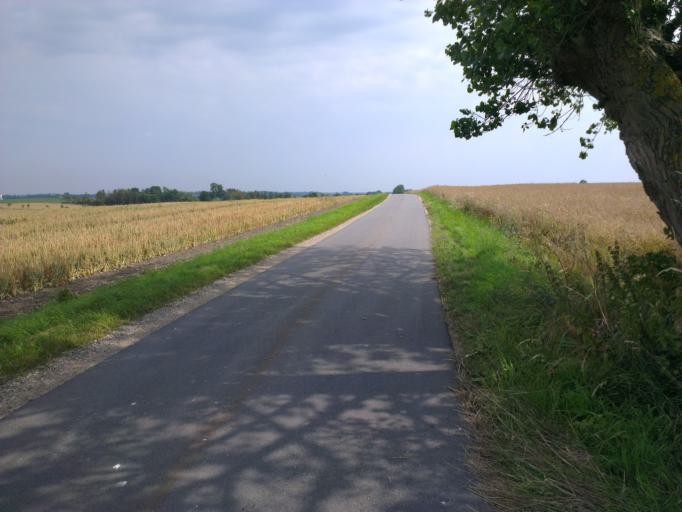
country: DK
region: Capital Region
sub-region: Frederikssund Kommune
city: Skibby
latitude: 55.7786
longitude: 11.9745
